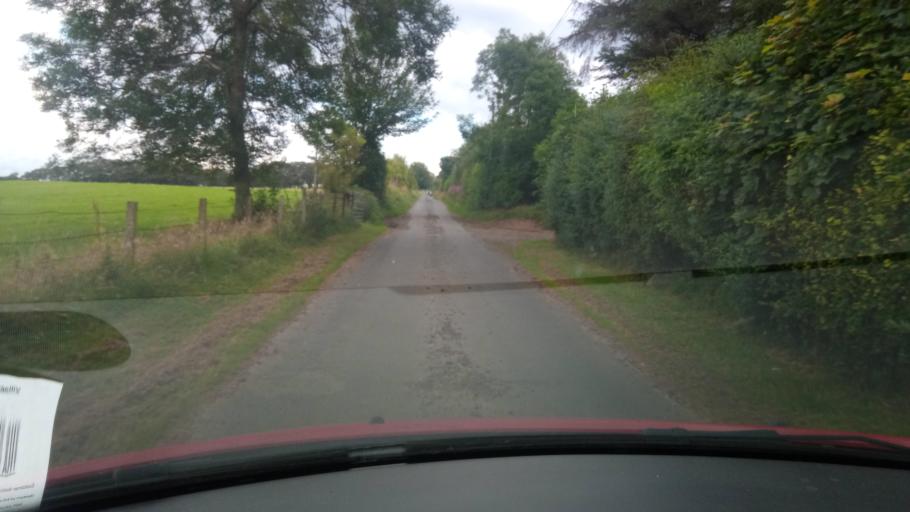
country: GB
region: Scotland
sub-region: The Scottish Borders
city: Jedburgh
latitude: 55.4086
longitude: -2.6170
